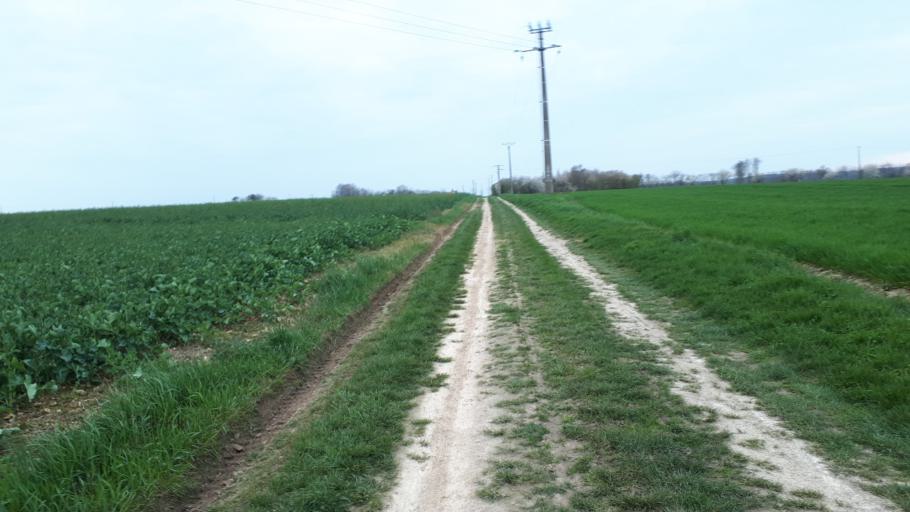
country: FR
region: Centre
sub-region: Departement du Loir-et-Cher
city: Aze
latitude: 47.8380
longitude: 1.0135
